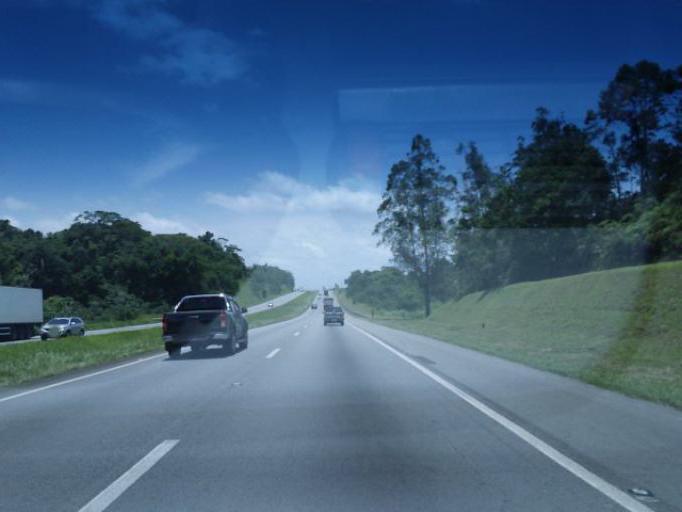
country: BR
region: Sao Paulo
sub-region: Registro
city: Registro
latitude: -24.4486
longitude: -47.8064
